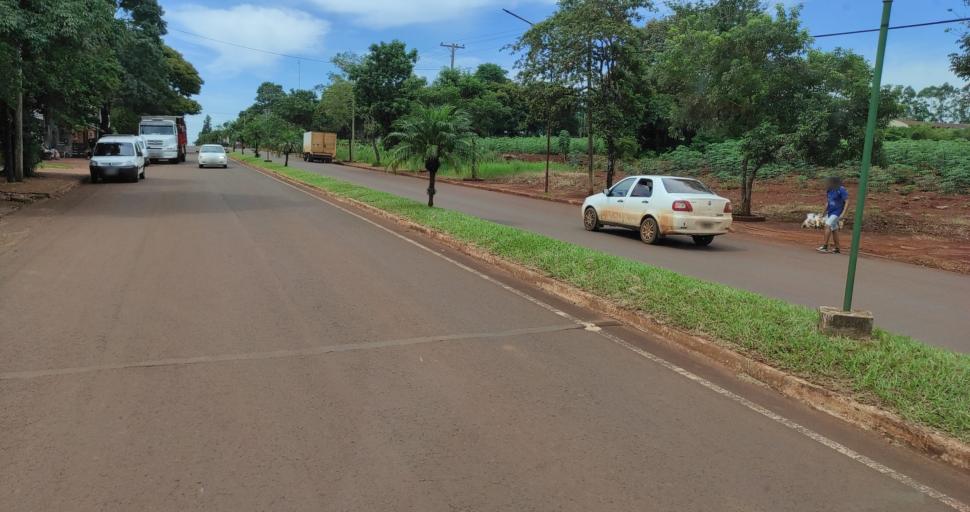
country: AR
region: Misiones
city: El Alcazar
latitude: -26.7118
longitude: -54.8155
